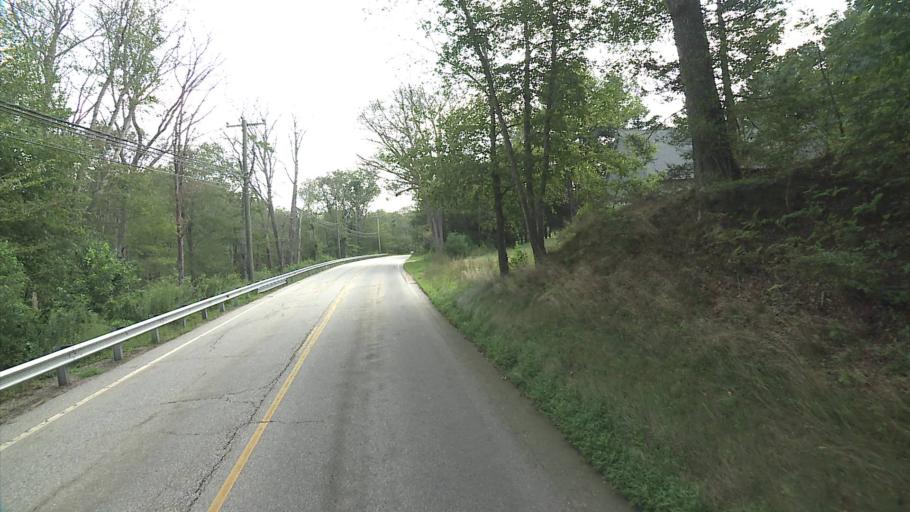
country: US
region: Connecticut
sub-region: Middlesex County
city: Deep River Center
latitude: 41.4227
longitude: -72.3934
